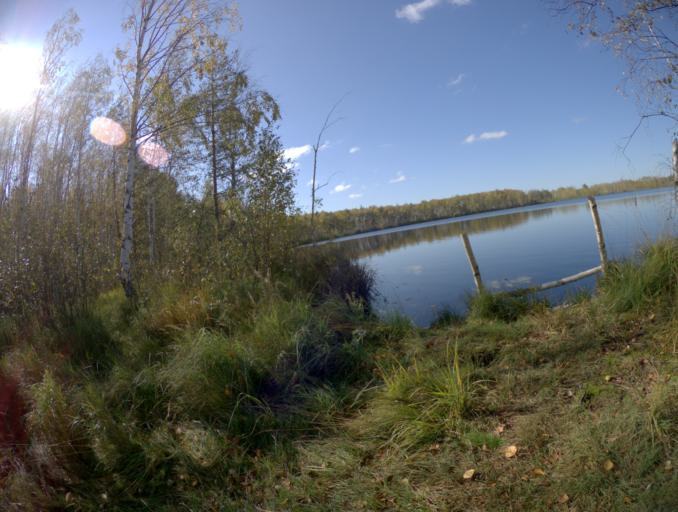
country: RU
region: Vladimir
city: Kameshkovo
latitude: 56.3326
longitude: 40.8167
